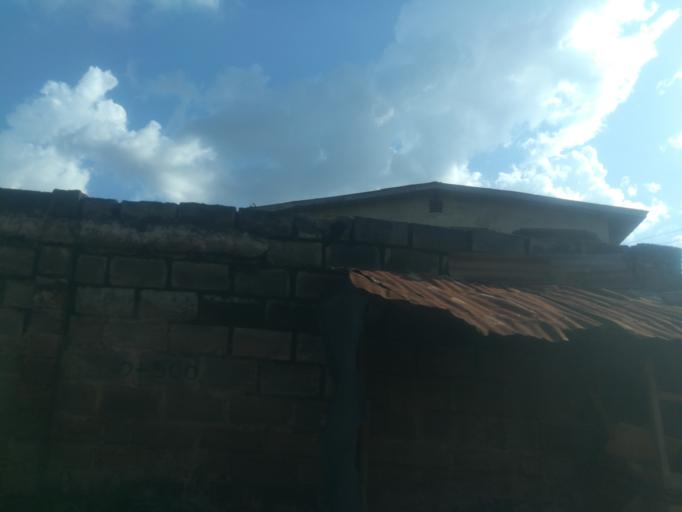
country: NG
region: Oyo
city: Ibadan
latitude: 7.4367
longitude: 3.9513
